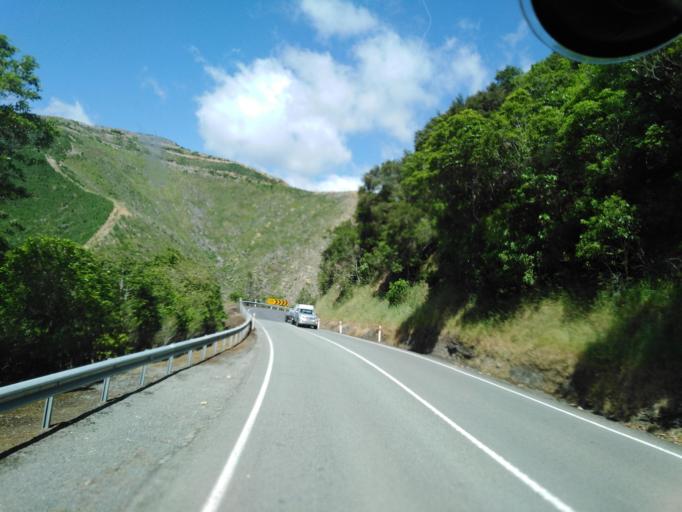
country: NZ
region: Nelson
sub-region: Nelson City
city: Nelson
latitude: -41.2302
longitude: 173.4143
